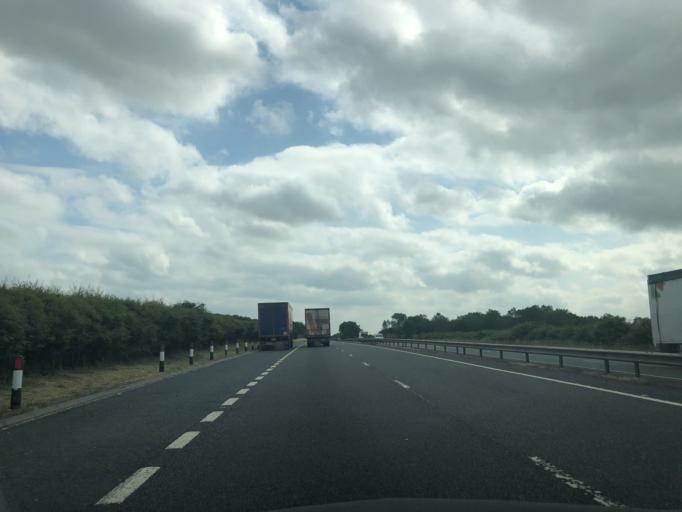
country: GB
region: England
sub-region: Stockton-on-Tees
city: Yarm
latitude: 54.4481
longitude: -1.3226
